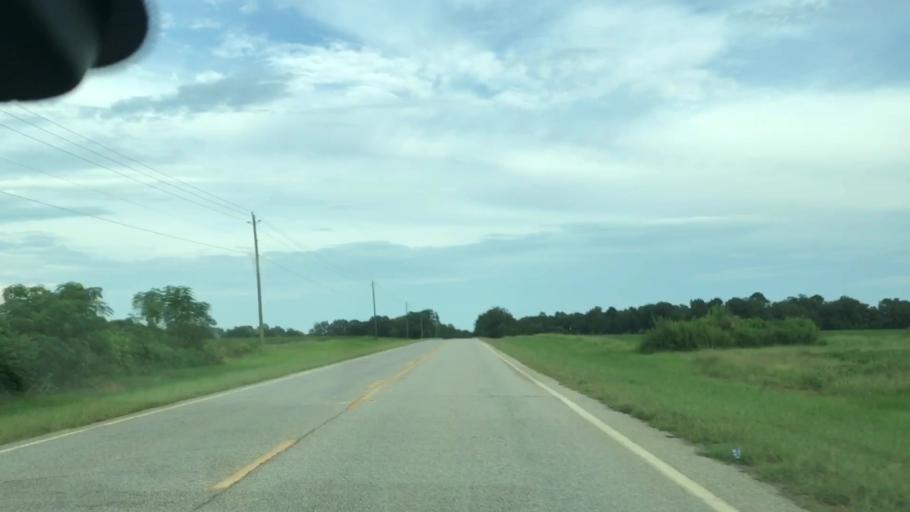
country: US
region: Georgia
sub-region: Quitman County
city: Georgetown
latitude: 31.7589
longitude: -85.0707
